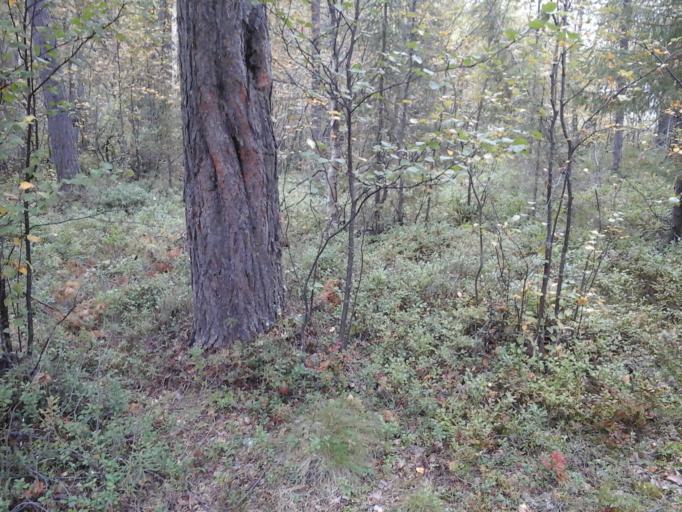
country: RU
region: Murmansk
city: Apatity
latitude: 67.5271
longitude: 33.2276
